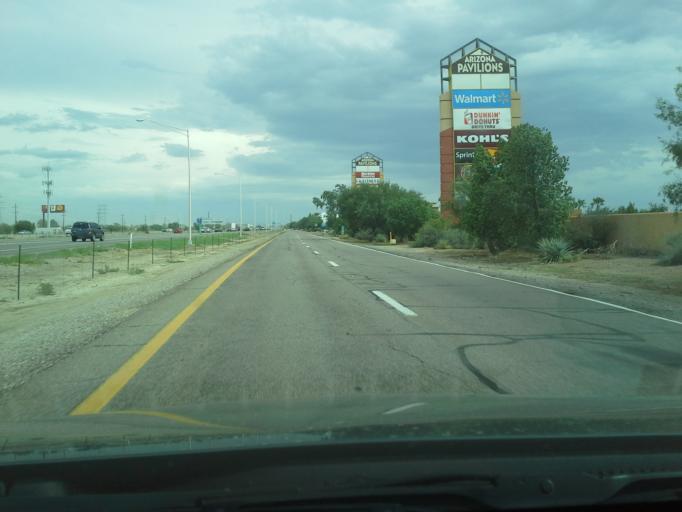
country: US
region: Arizona
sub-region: Pima County
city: Tortolita
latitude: 32.3560
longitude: -111.0877
